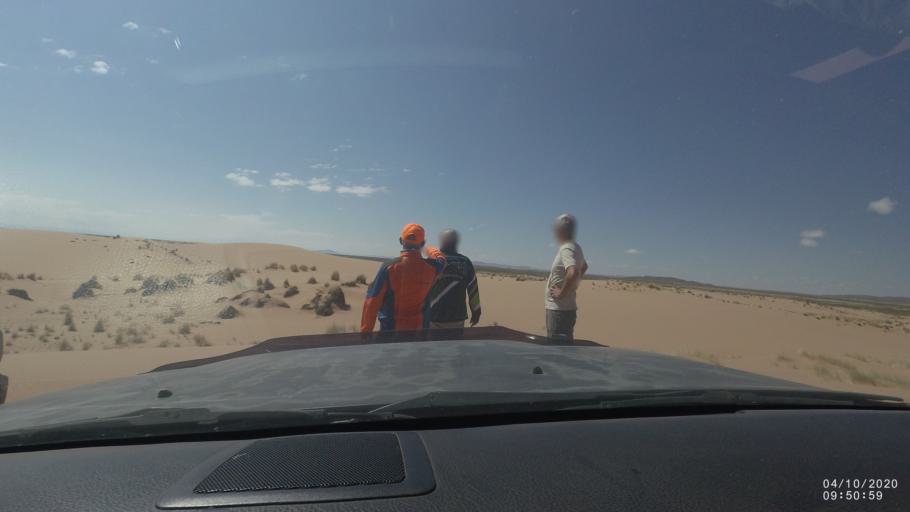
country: BO
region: Oruro
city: Poopo
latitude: -18.7065
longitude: -67.4978
